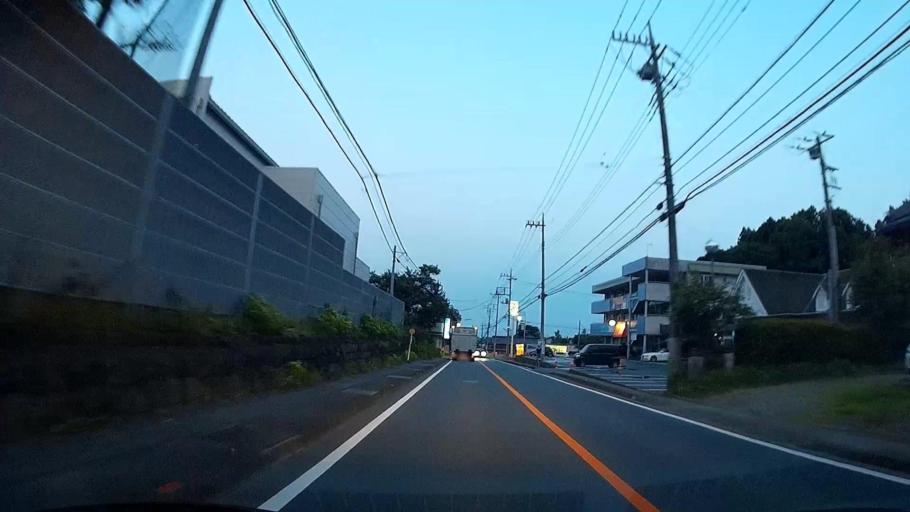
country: JP
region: Gunma
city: Annaka
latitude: 36.3740
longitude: 138.8972
